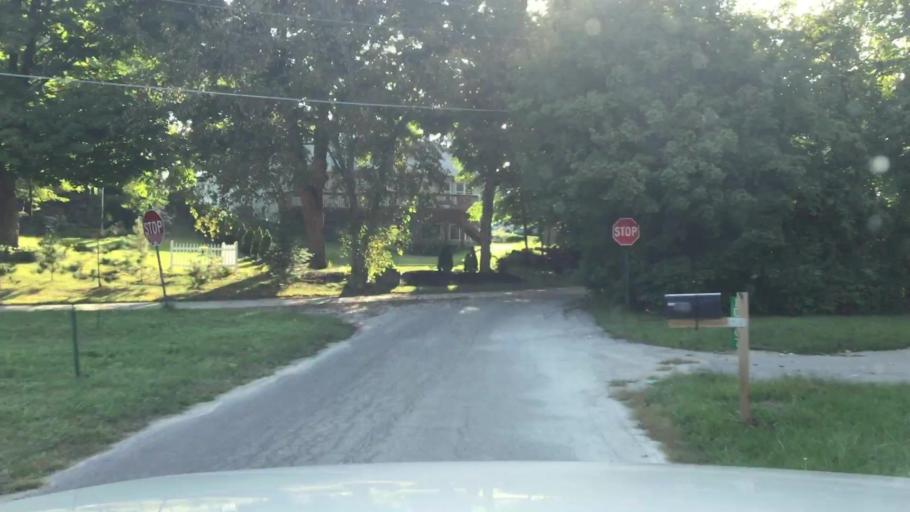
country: US
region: Michigan
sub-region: Livingston County
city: Whitmore Lake
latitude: 42.4441
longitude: -83.8343
